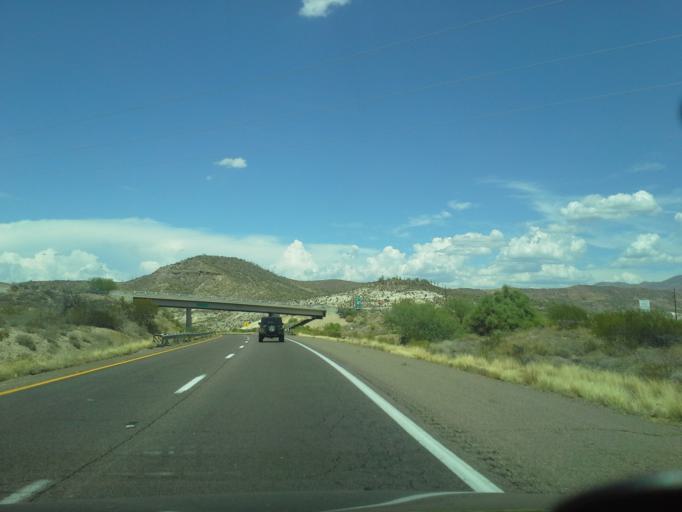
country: US
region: Arizona
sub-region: Maricopa County
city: New River
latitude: 33.9670
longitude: -112.1280
